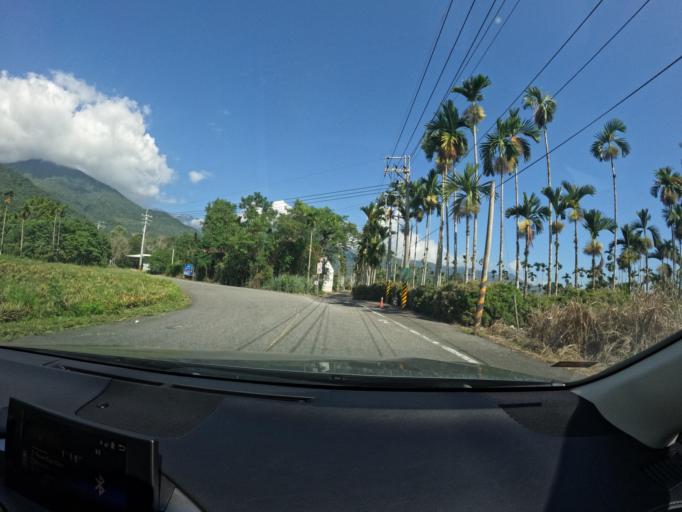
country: TW
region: Taiwan
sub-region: Hualien
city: Hualian
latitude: 23.5609
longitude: 121.3794
